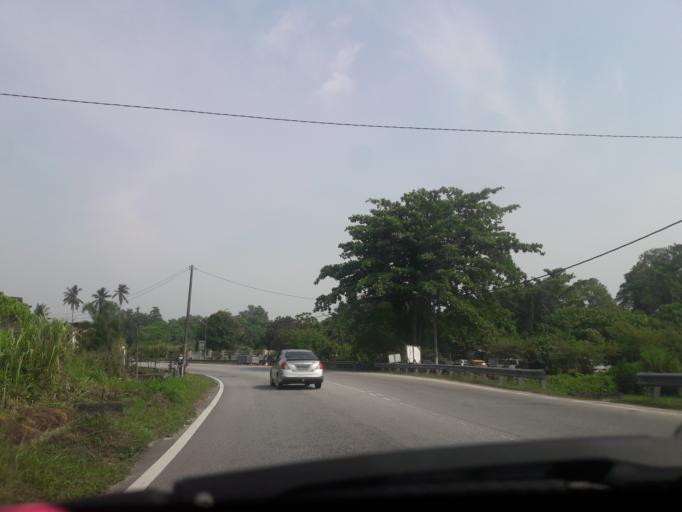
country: MY
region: Kedah
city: Kulim
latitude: 5.3667
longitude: 100.5495
